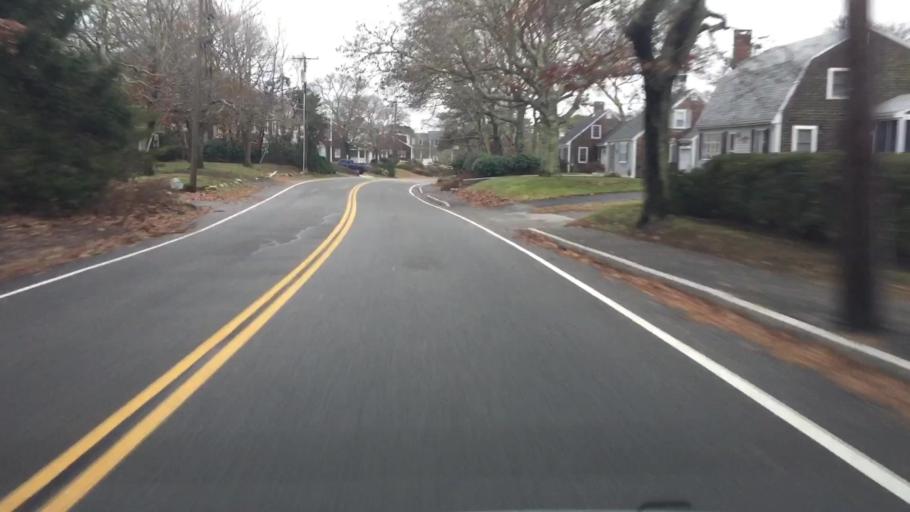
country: US
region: Massachusetts
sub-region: Barnstable County
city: West Falmouth
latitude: 41.6284
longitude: -70.6350
